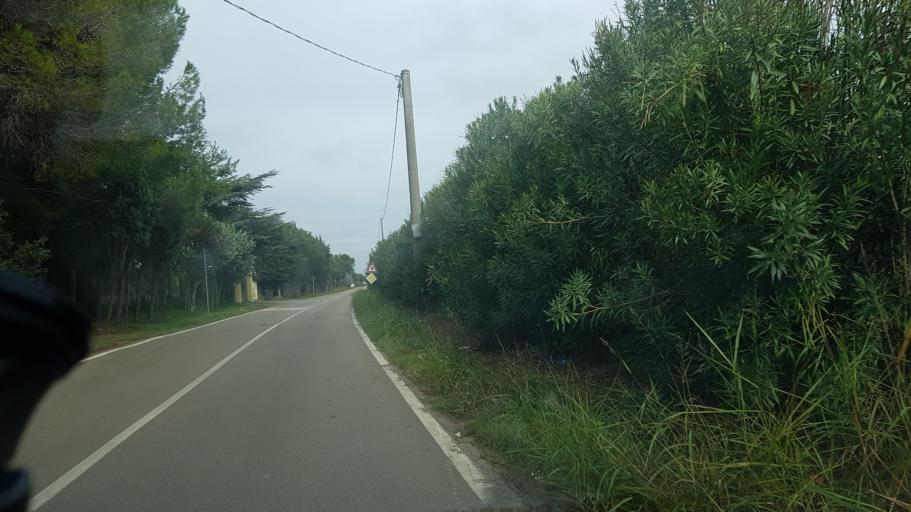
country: IT
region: Apulia
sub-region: Provincia di Lecce
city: Guagnano
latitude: 40.4067
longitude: 17.9500
